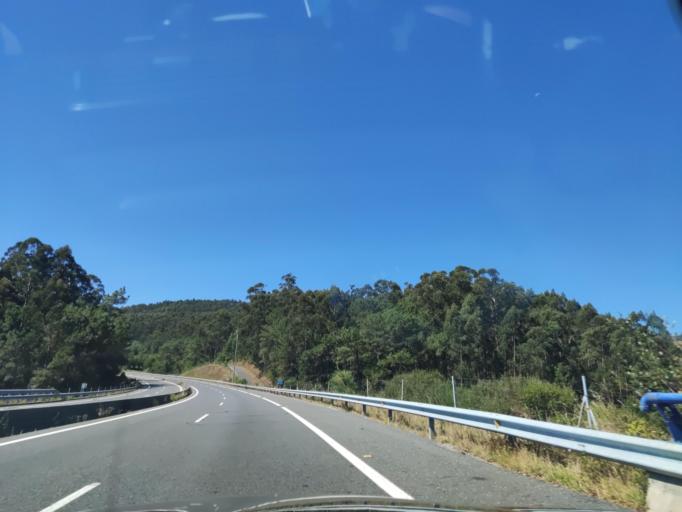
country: ES
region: Galicia
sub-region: Provincia da Coruna
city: Boiro
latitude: 42.6564
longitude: -8.8976
